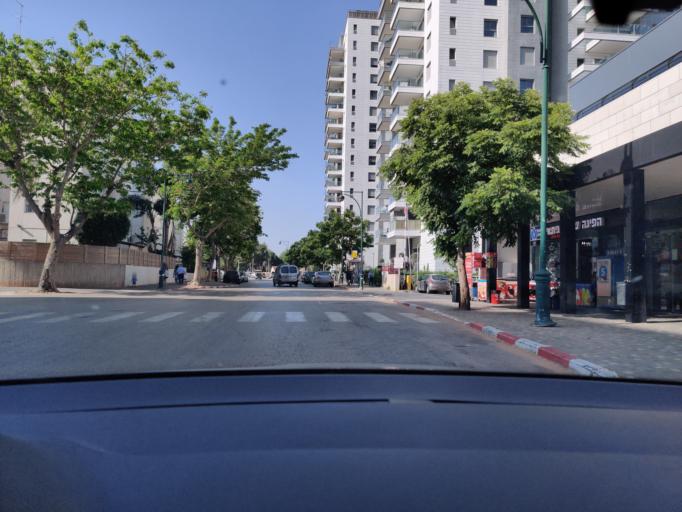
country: IL
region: Haifa
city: Hadera
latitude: 32.4675
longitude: 34.9528
